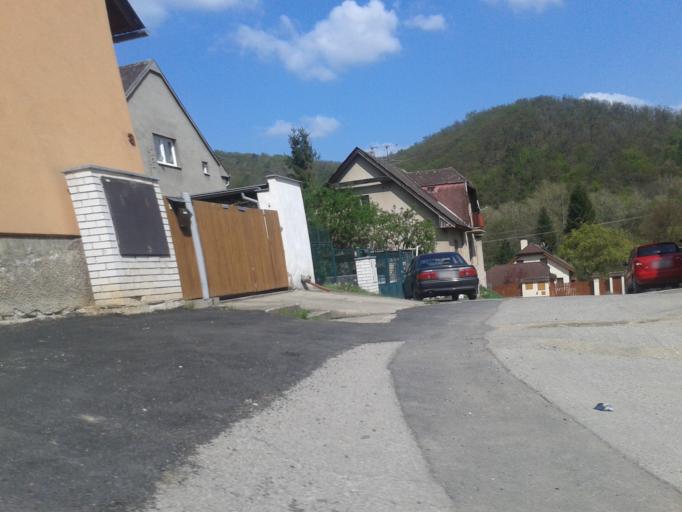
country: CZ
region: Central Bohemia
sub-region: Okres Beroun
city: Lodenice
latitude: 50.0035
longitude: 14.1529
